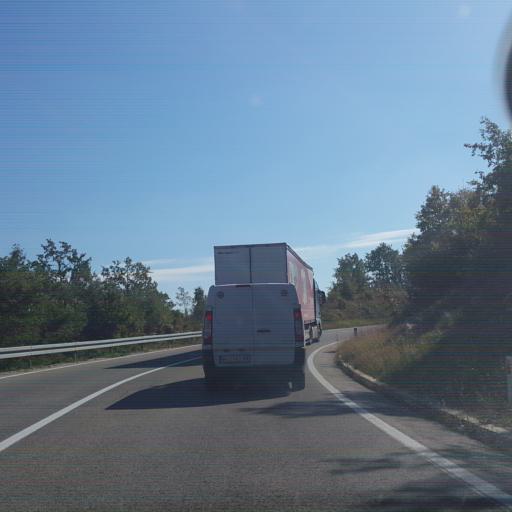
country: RS
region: Central Serbia
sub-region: Nisavski Okrug
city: Svrljig
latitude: 43.4524
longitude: 22.1800
